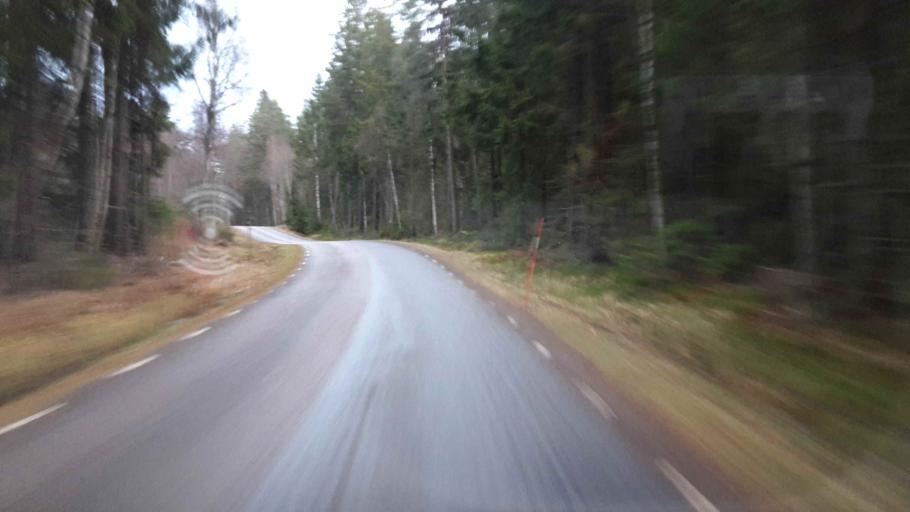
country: SE
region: Kalmar
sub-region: Vasterviks Kommun
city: Overum
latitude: 58.1507
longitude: 16.2398
